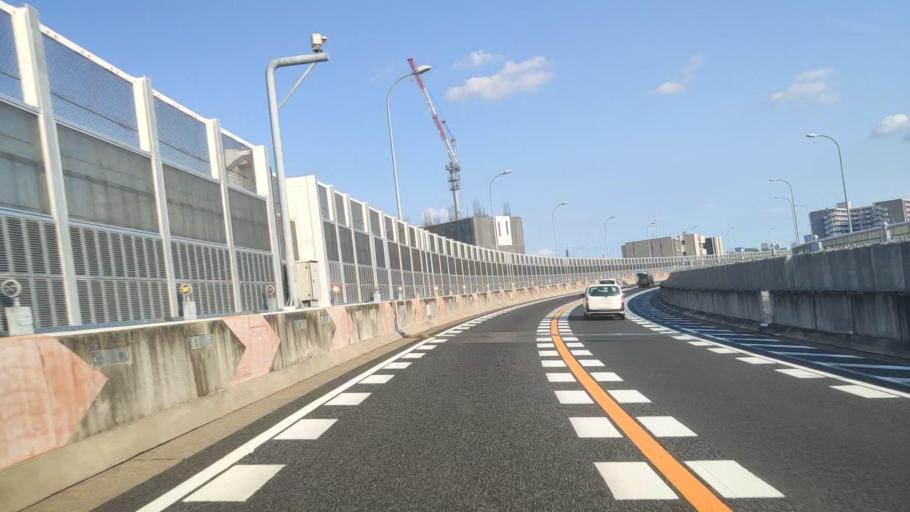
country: JP
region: Aichi
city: Nagoya-shi
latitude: 35.2022
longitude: 136.8905
